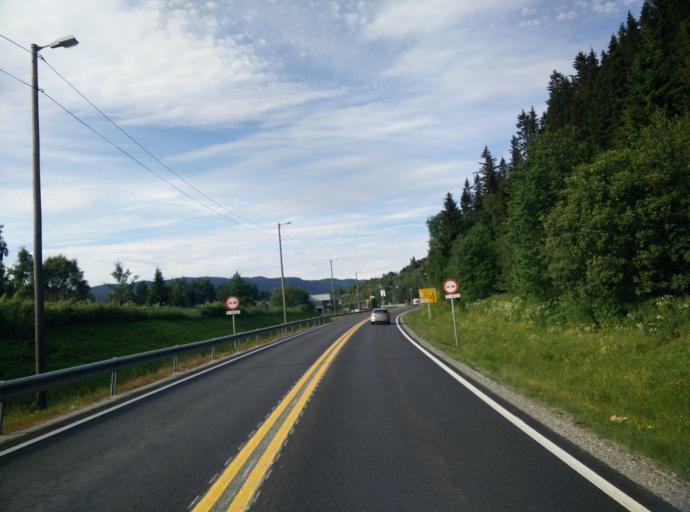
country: NO
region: Sor-Trondelag
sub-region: Orkdal
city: Orkanger
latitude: 63.2933
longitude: 9.8525
